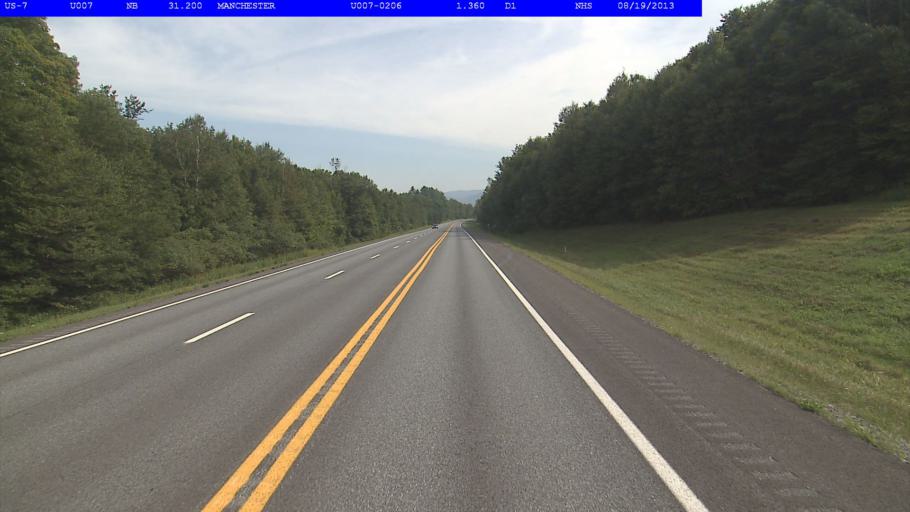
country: US
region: Vermont
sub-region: Bennington County
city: Manchester Center
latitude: 43.1330
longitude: -73.0635
